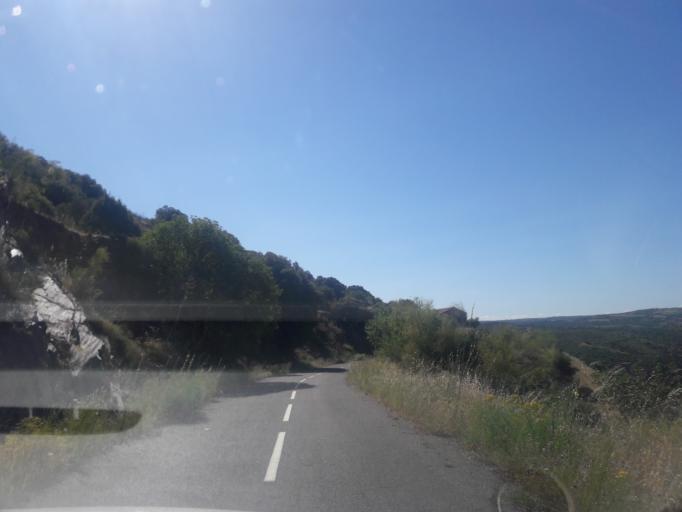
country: ES
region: Castille and Leon
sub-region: Provincia de Salamanca
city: Saucelle
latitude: 41.0317
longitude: -6.7580
